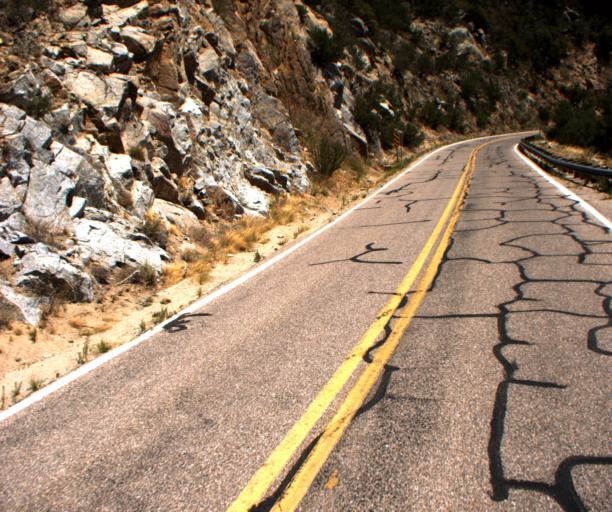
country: US
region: Arizona
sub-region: Pima County
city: Sells
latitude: 31.9615
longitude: -111.6014
